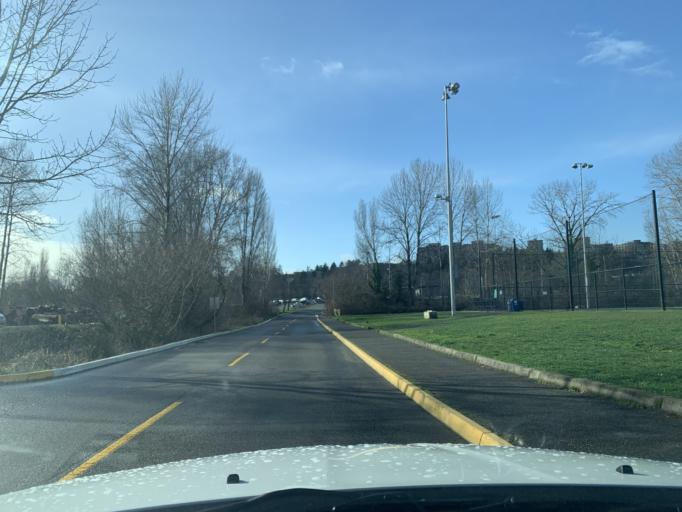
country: US
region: Washington
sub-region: King County
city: Seattle
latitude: 47.6594
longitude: -122.2946
